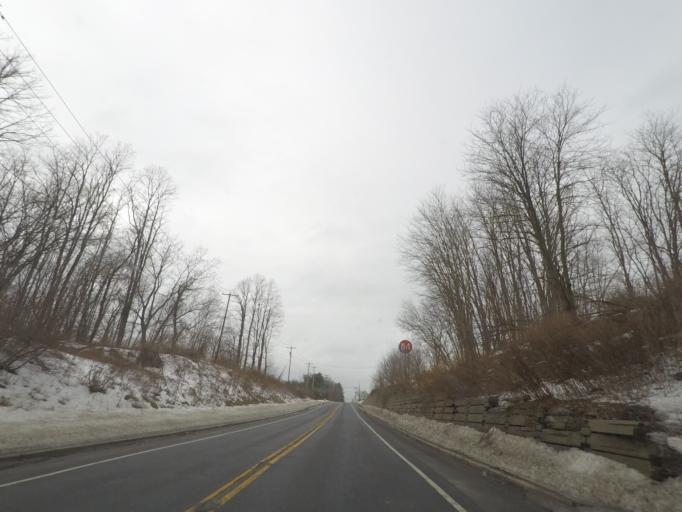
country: US
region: New York
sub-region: Schenectady County
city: Rotterdam
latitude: 42.7257
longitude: -73.9606
